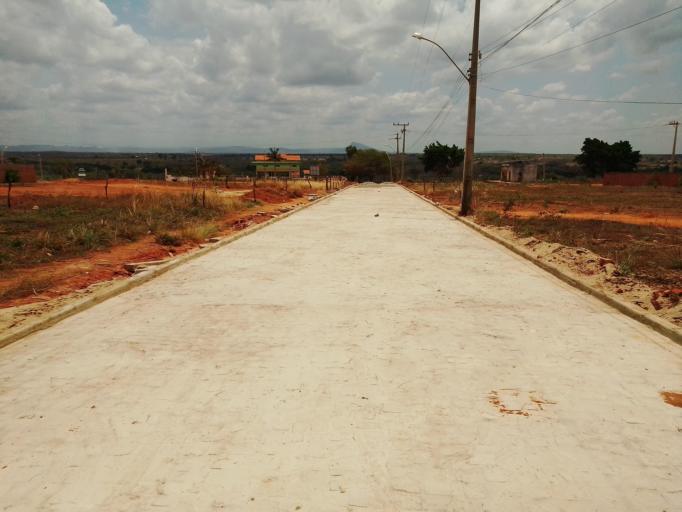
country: BR
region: Minas Gerais
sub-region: Sao Joao Do Paraiso
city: Sao Joao do Paraiso
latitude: -15.0296
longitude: -41.9318
